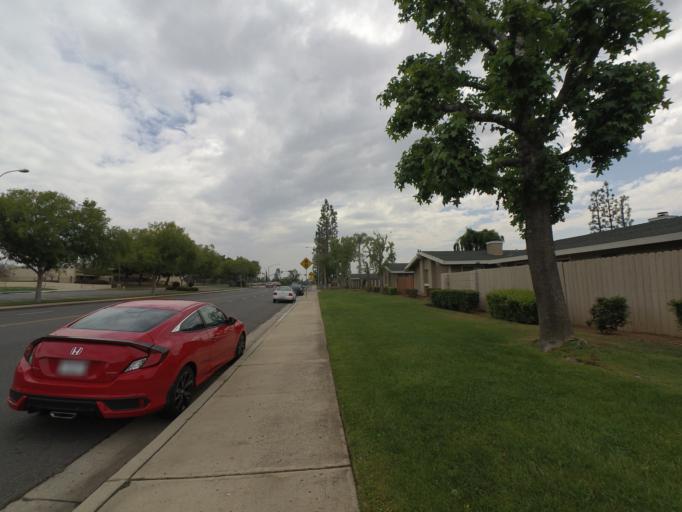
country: US
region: California
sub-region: Riverside County
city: Moreno Valley
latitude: 33.9317
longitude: -117.2457
